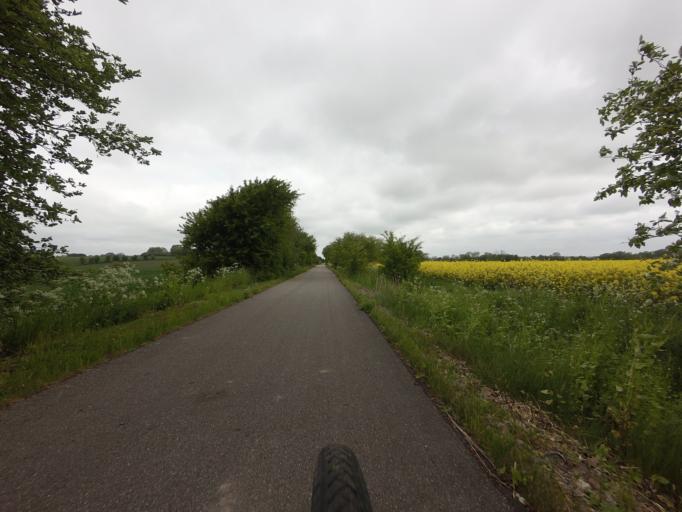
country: DK
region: Zealand
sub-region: Slagelse Kommune
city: Slagelse
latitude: 55.3313
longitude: 11.3980
